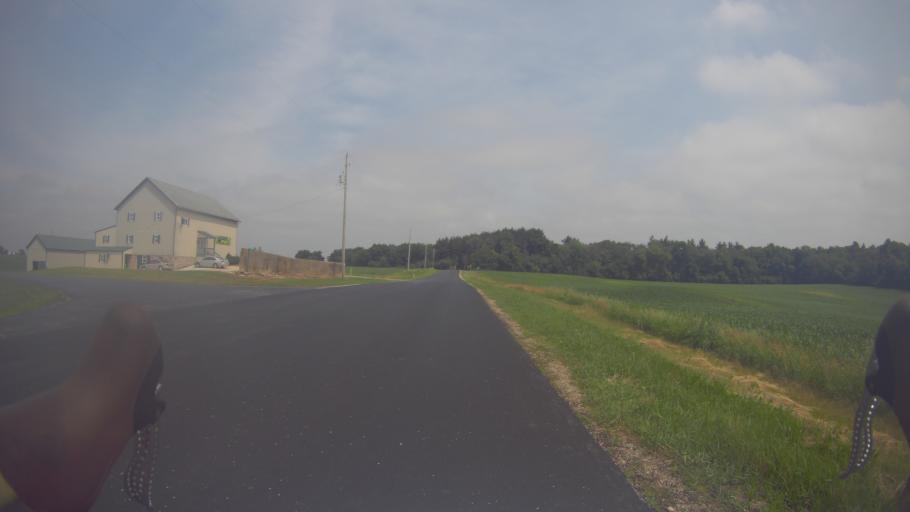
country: US
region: Wisconsin
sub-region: Rock County
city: Edgerton
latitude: 42.8928
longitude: -89.0405
